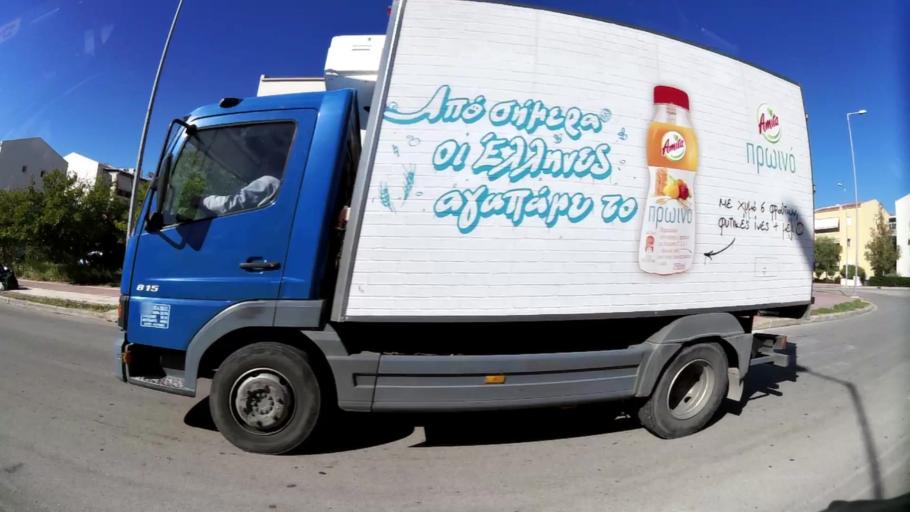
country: GR
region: Attica
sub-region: Nomarchia Anatolikis Attikis
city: Thrakomakedones
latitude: 38.1139
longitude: 23.7709
